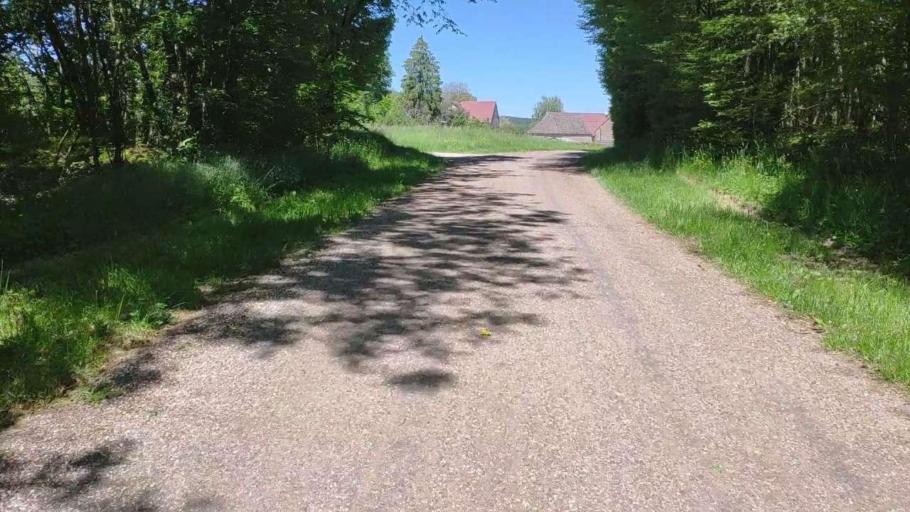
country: FR
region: Franche-Comte
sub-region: Departement du Jura
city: Poligny
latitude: 46.7417
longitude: 5.6736
